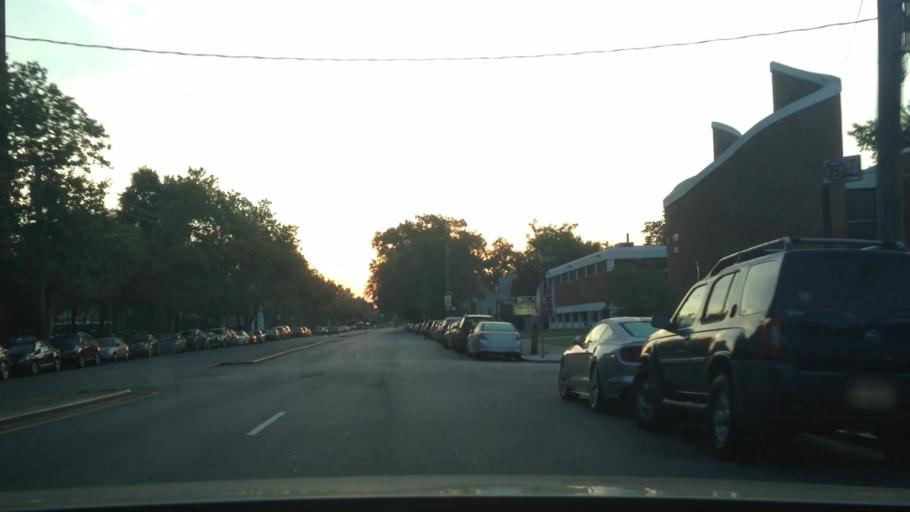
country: US
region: New York
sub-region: Queens County
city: Jamaica
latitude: 40.6722
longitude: -73.7733
